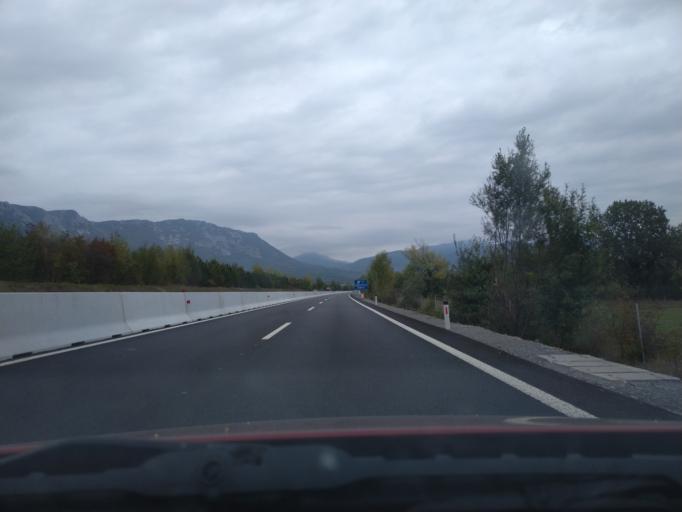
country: SI
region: Ajdovscina
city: Lokavec
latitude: 45.8844
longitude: 13.8796
